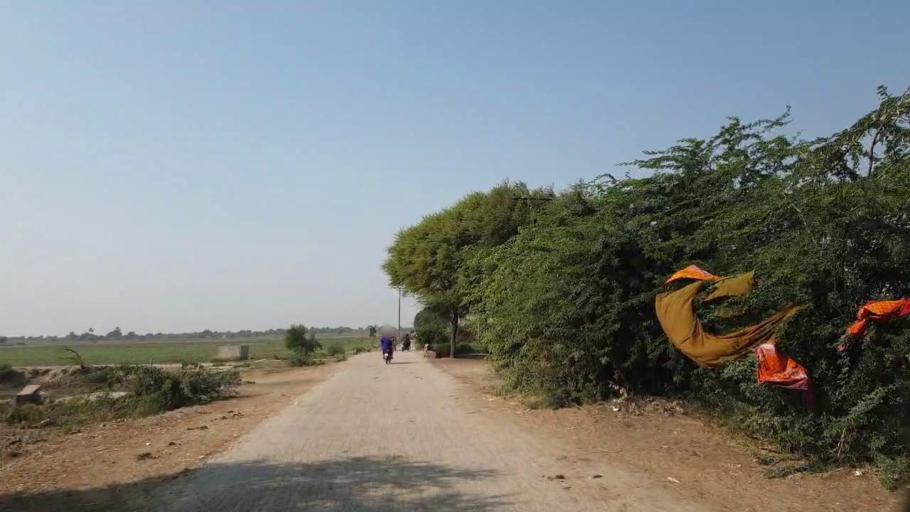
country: PK
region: Sindh
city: Bulri
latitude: 24.9539
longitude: 68.3391
